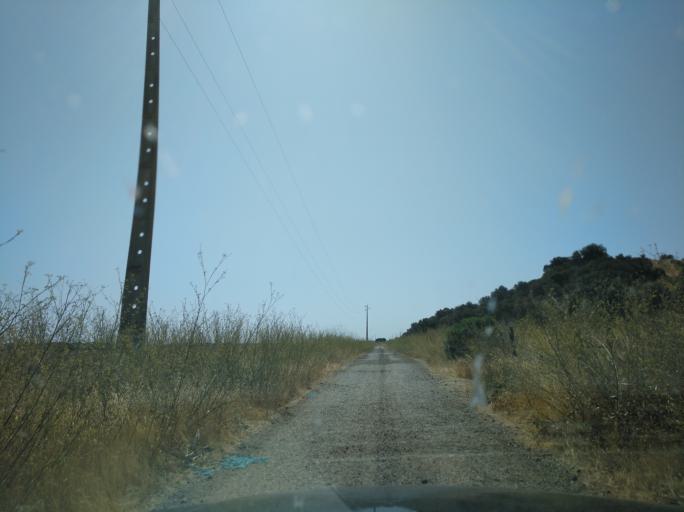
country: PT
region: Portalegre
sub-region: Campo Maior
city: Campo Maior
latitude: 39.0570
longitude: -7.0049
